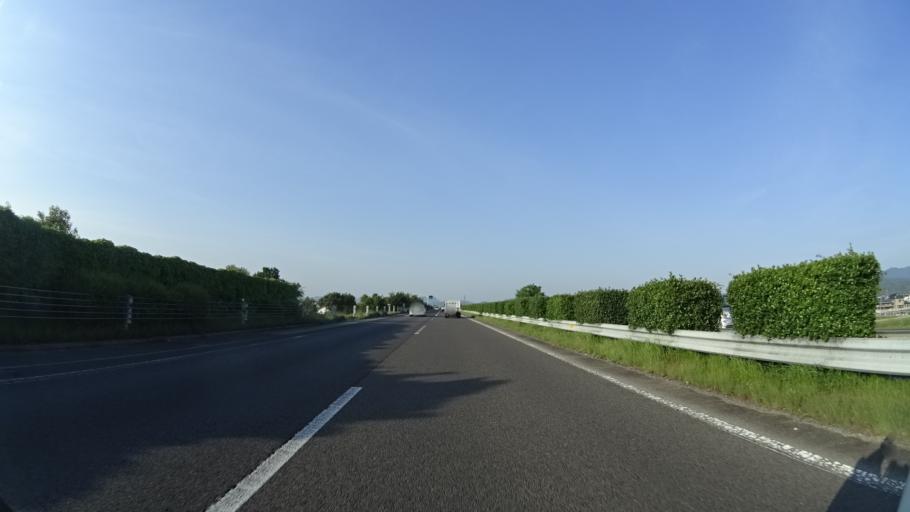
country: JP
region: Kagawa
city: Kan'onjicho
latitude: 34.0914
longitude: 133.6607
